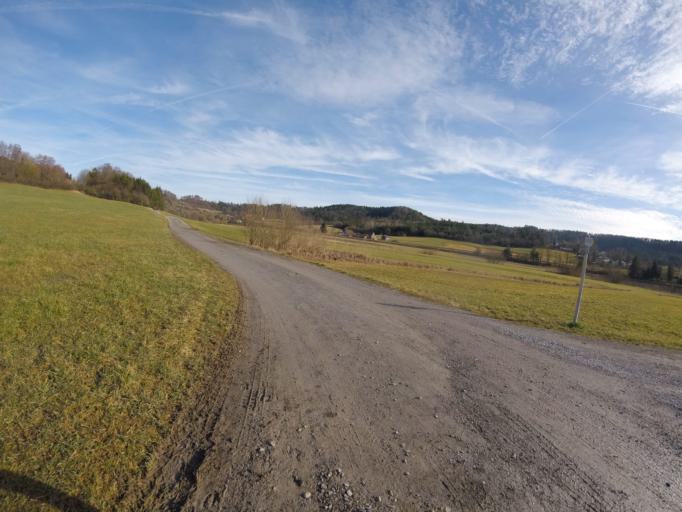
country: DE
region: Baden-Wuerttemberg
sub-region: Regierungsbezirk Stuttgart
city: Oberrot
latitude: 48.9824
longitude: 9.6608
